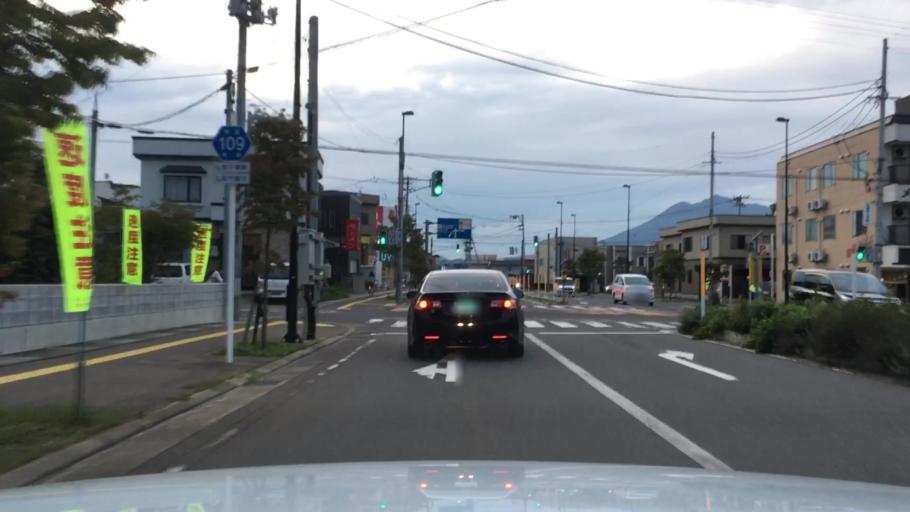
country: JP
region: Aomori
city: Hirosaki
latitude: 40.5916
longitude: 140.4746
